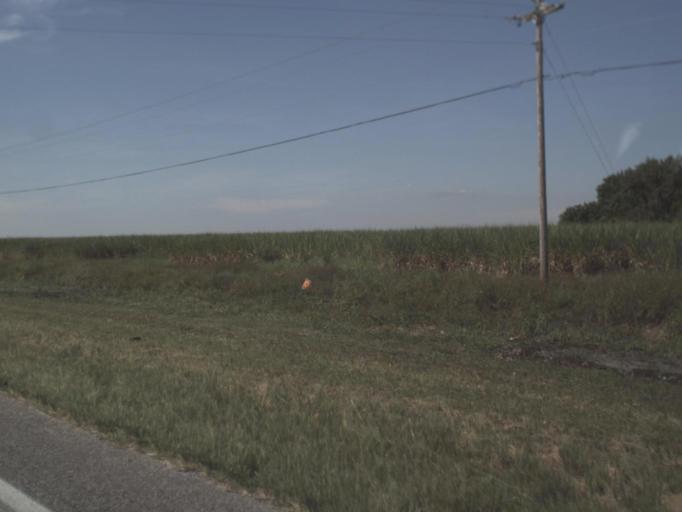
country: US
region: Florida
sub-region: Glades County
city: Moore Haven
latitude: 26.8339
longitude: -81.1293
